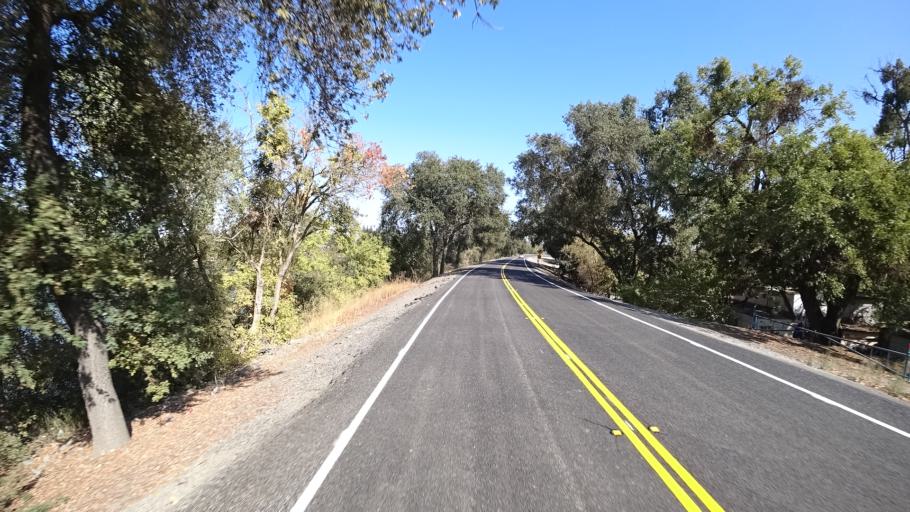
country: US
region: California
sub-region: Yolo County
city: West Sacramento
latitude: 38.6469
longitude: -121.5781
